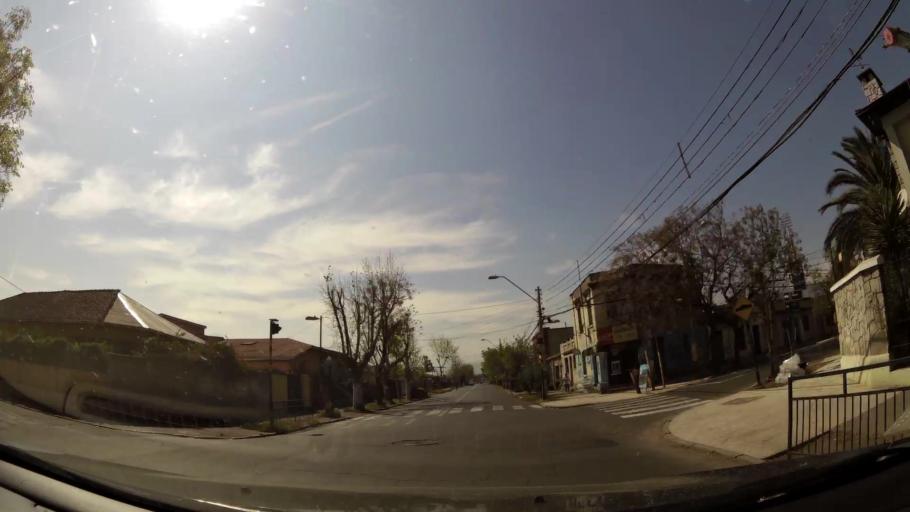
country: CL
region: Santiago Metropolitan
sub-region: Provincia de Santiago
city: Santiago
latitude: -33.4031
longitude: -70.6611
